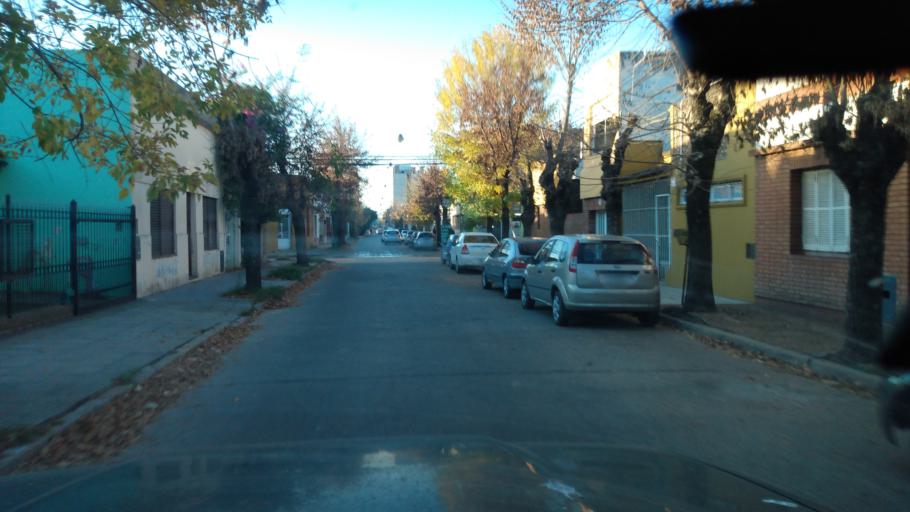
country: AR
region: Buenos Aires
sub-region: Partido de Lujan
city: Lujan
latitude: -34.5686
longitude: -59.1196
